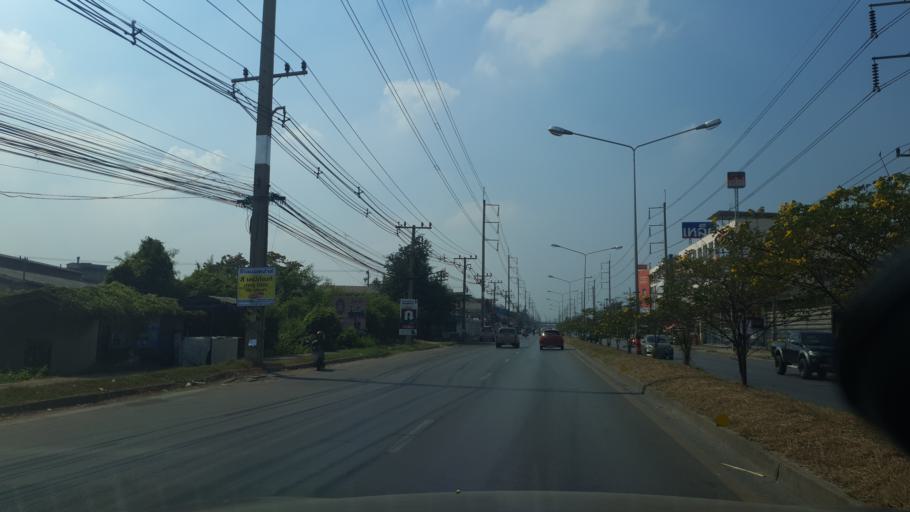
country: TH
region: Samut Sakhon
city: Krathum Baen
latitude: 13.6708
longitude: 100.2811
